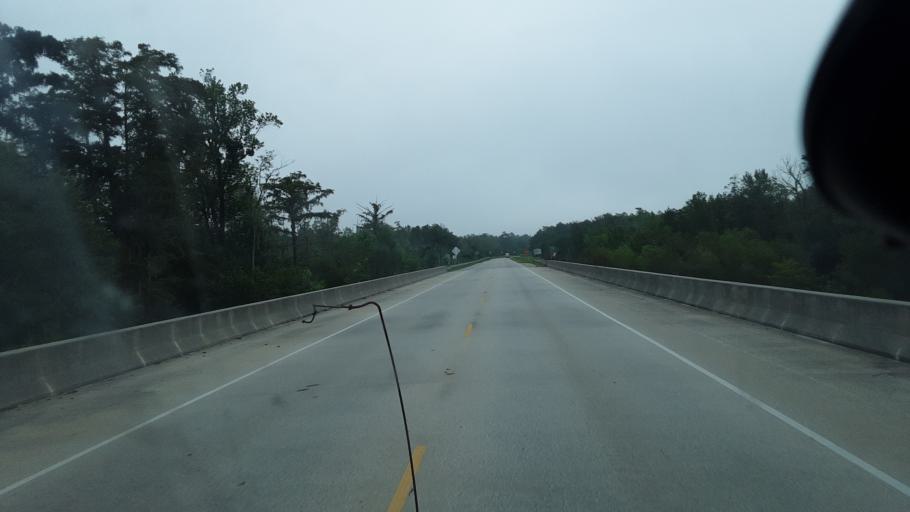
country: US
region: South Carolina
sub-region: Florence County
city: Johnsonville
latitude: 33.9096
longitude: -79.4272
